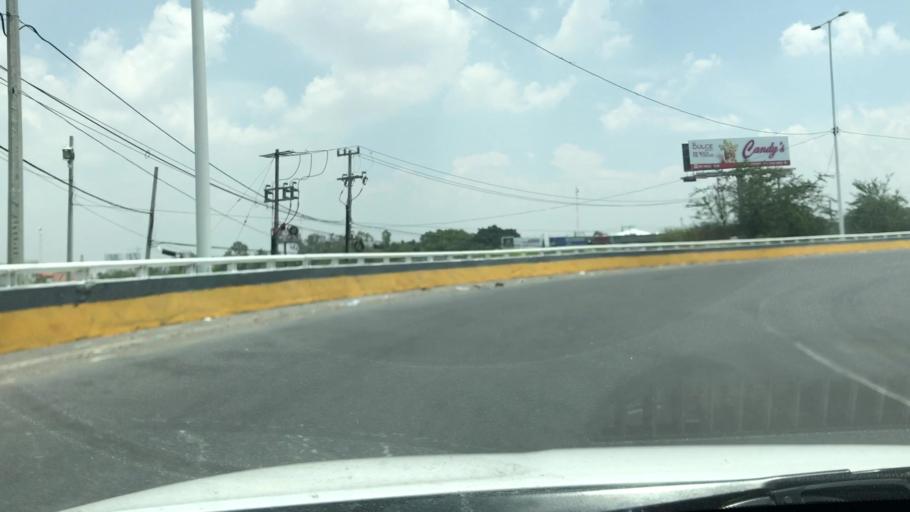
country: MX
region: Jalisco
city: Zapopan2
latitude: 20.6958
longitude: -103.4536
